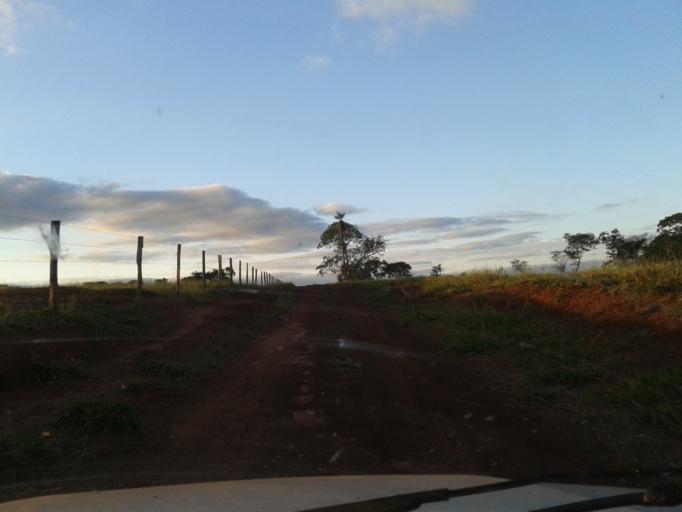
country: BR
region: Minas Gerais
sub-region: Campina Verde
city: Campina Verde
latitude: -19.4946
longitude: -49.6785
